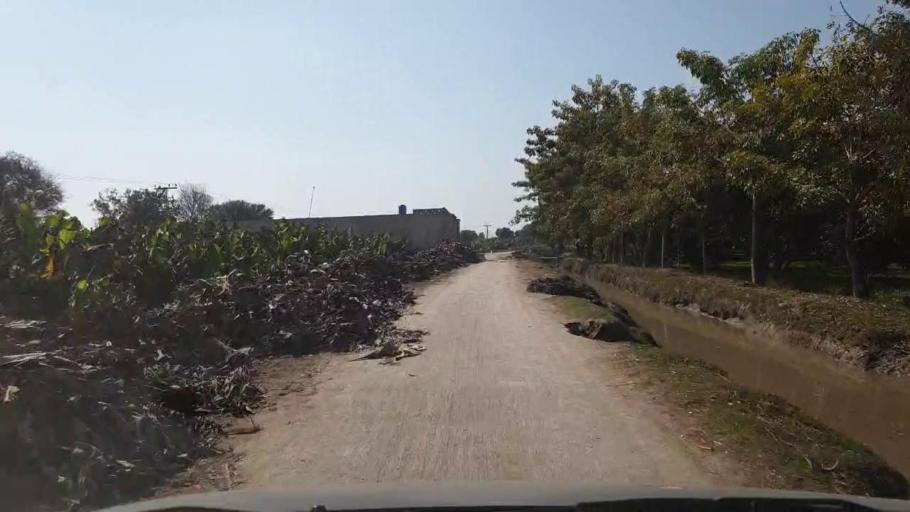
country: PK
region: Sindh
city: Tando Allahyar
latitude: 25.4287
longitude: 68.6361
